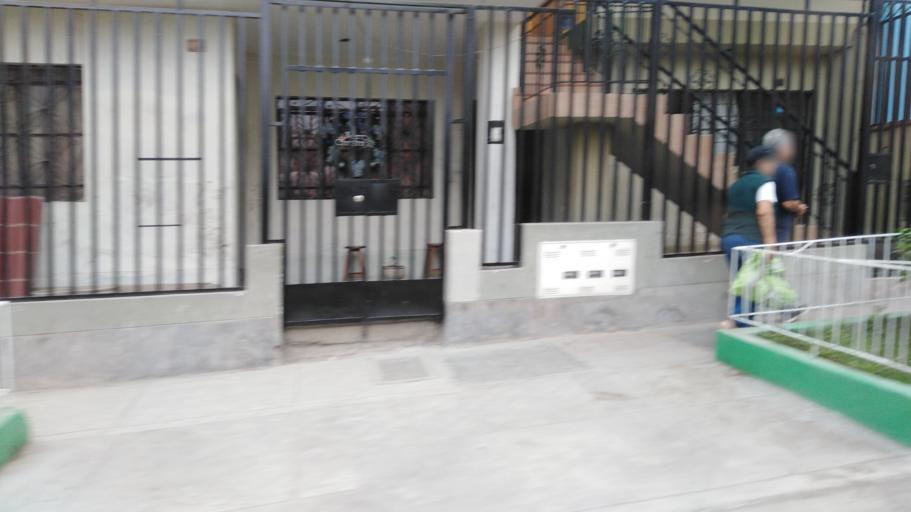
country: PE
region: Lima
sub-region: Lima
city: Surco
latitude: -12.1435
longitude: -76.9460
